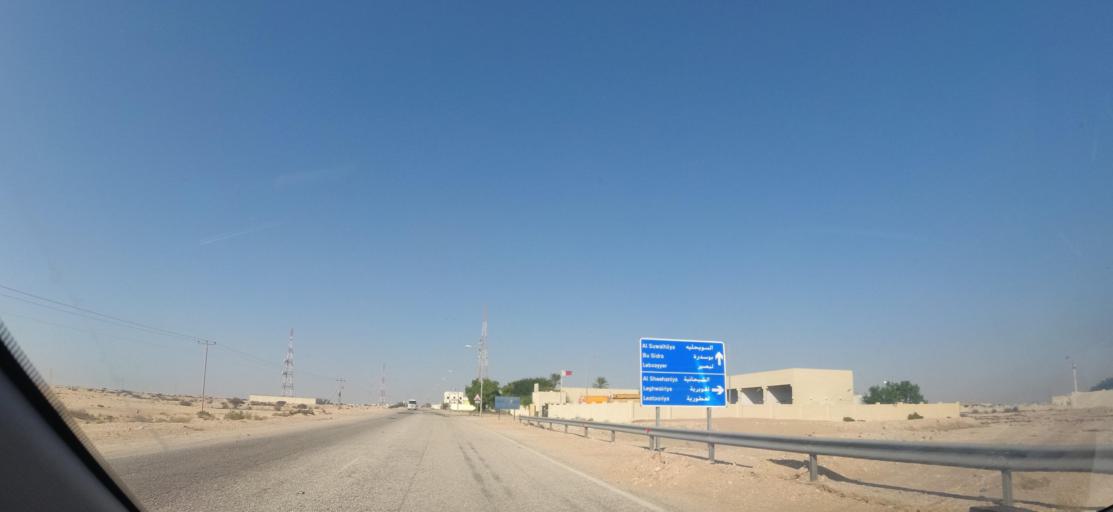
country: QA
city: Al Jumayliyah
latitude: 25.6158
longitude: 51.0789
